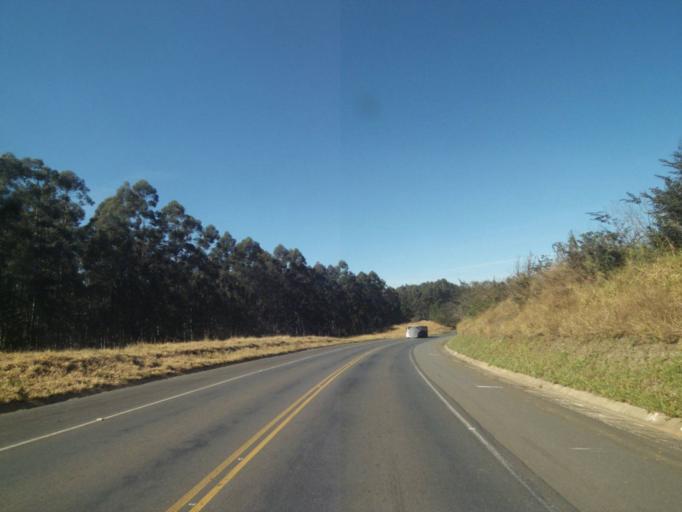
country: BR
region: Parana
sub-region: Tibagi
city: Tibagi
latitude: -24.5128
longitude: -50.4377
